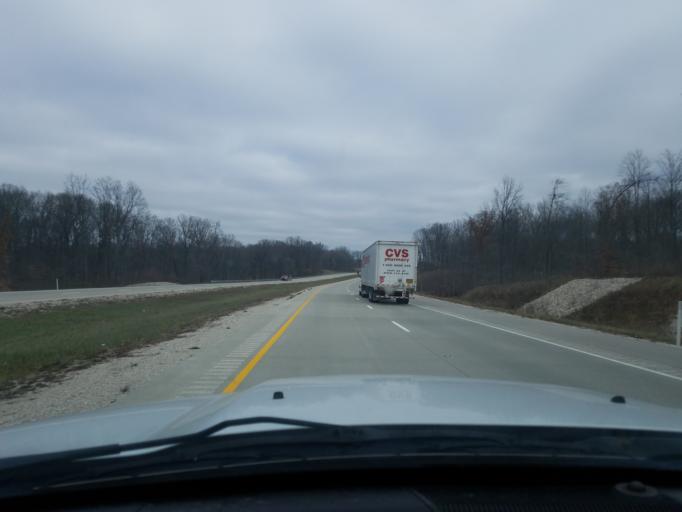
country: US
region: Indiana
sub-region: Greene County
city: Bloomfield
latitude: 38.9497
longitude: -86.8619
